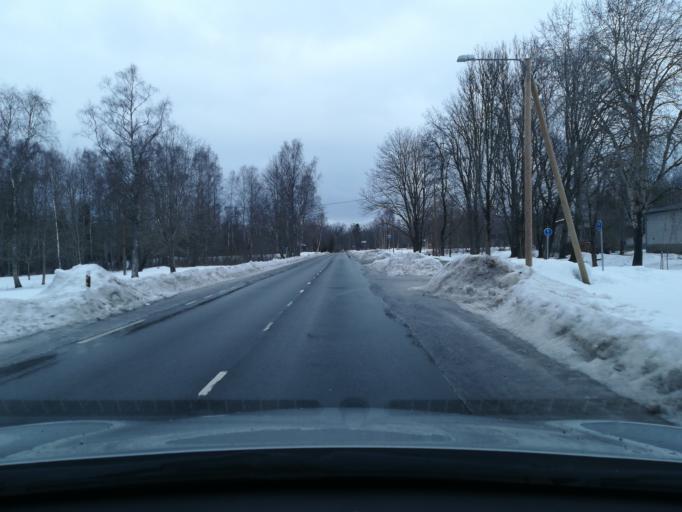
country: EE
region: Harju
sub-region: Nissi vald
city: Turba
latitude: 59.0746
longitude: 24.2409
